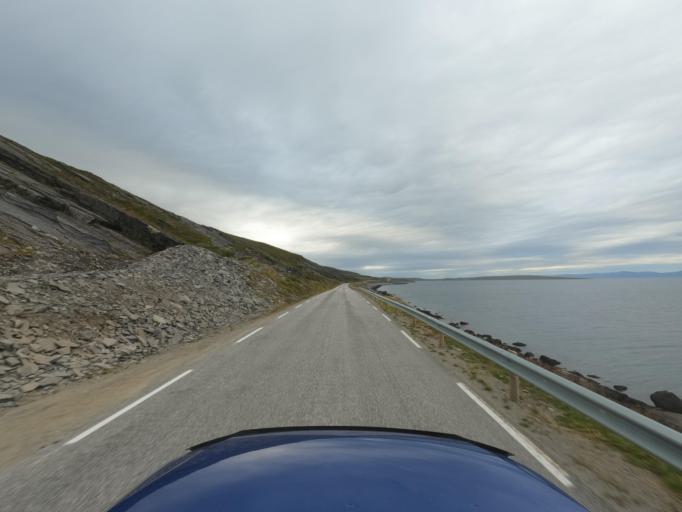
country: NO
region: Finnmark Fylke
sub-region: Nordkapp
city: Honningsvag
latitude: 70.7113
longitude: 25.5627
